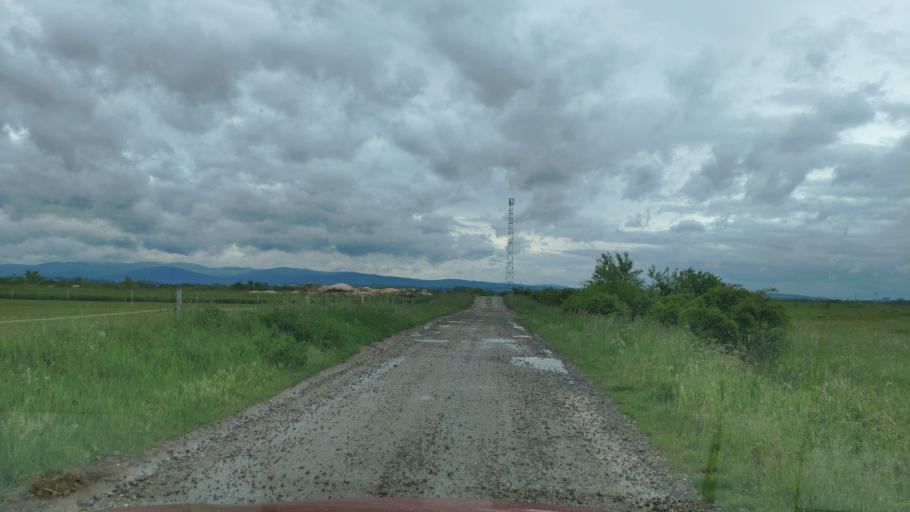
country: SK
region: Kosicky
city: Moldava nad Bodvou
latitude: 48.5434
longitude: 21.1126
